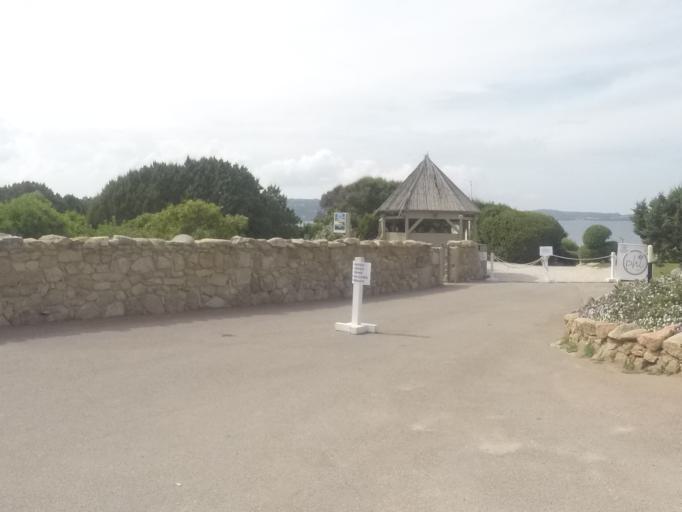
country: IT
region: Sardinia
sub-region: Provincia di Olbia-Tempio
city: Porto Cervo
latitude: 41.1417
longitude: 9.4674
